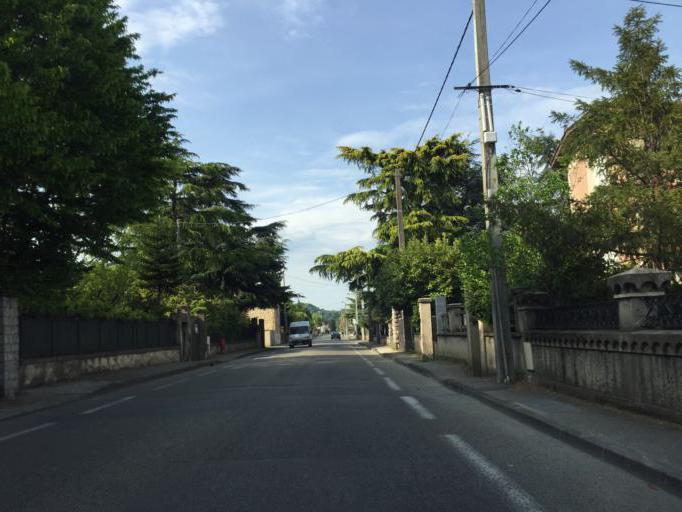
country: FR
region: Rhone-Alpes
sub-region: Departement de la Drome
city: Romans-sur-Isere
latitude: 45.0565
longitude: 5.0495
